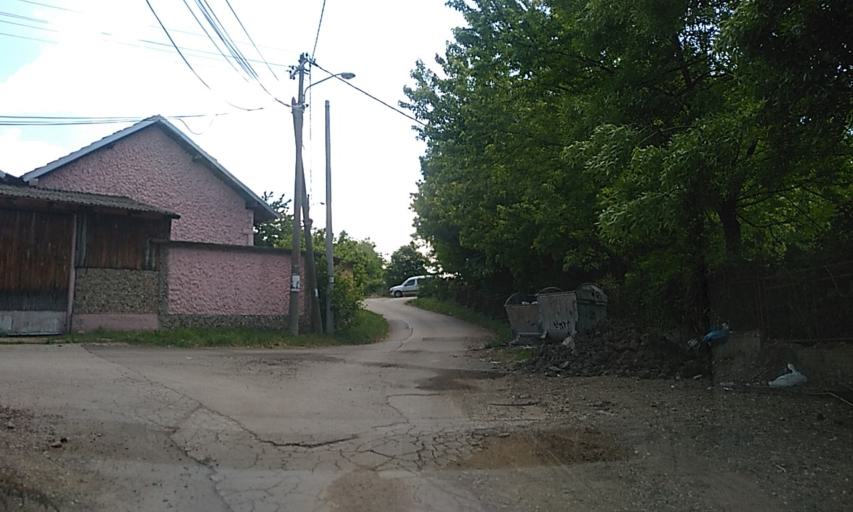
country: RS
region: Central Serbia
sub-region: Nisavski Okrug
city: Niska Banja
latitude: 43.3676
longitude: 21.9955
